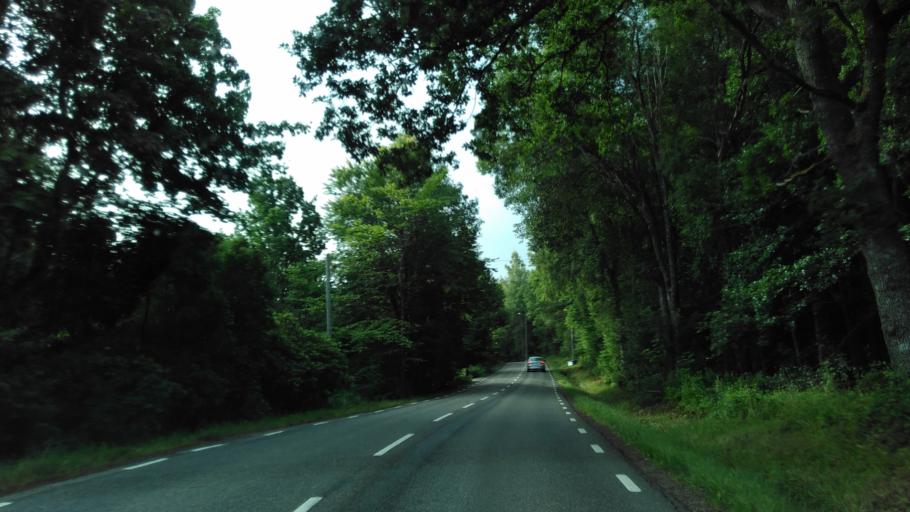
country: SE
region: Vaestra Goetaland
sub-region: Boras Kommun
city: Ganghester
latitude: 57.7931
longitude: 13.0138
